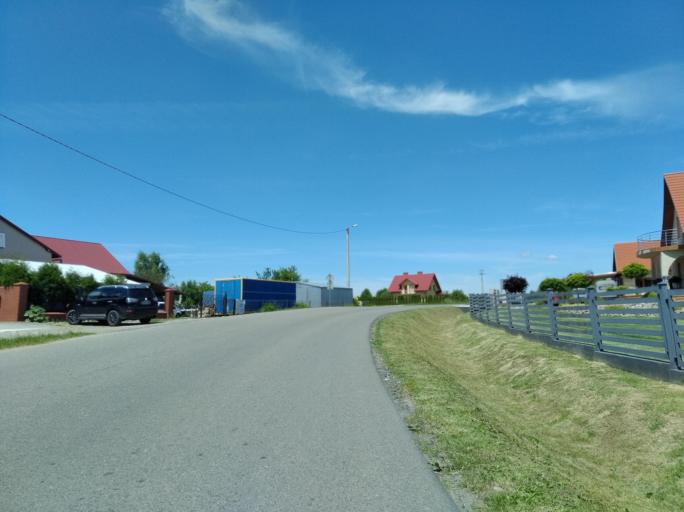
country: PL
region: Subcarpathian Voivodeship
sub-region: Powiat jasielski
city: Osiek Jasielski
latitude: 49.6722
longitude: 21.5433
